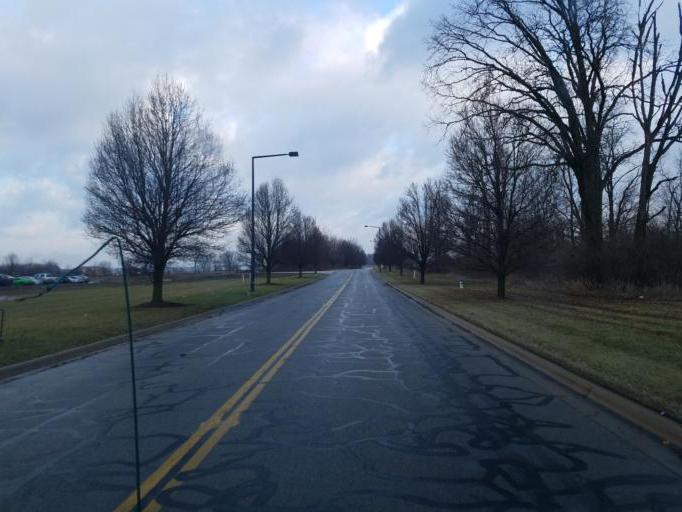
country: US
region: Ohio
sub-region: Marion County
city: Marion
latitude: 40.6106
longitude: -83.1408
